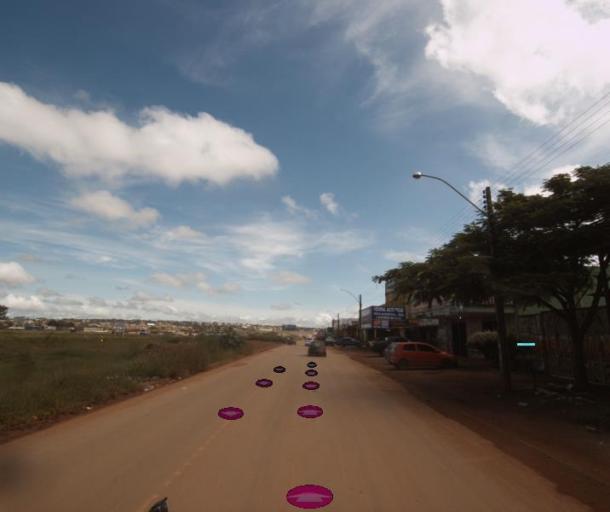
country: BR
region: Federal District
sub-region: Brasilia
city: Brasilia
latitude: -15.7481
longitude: -48.2630
